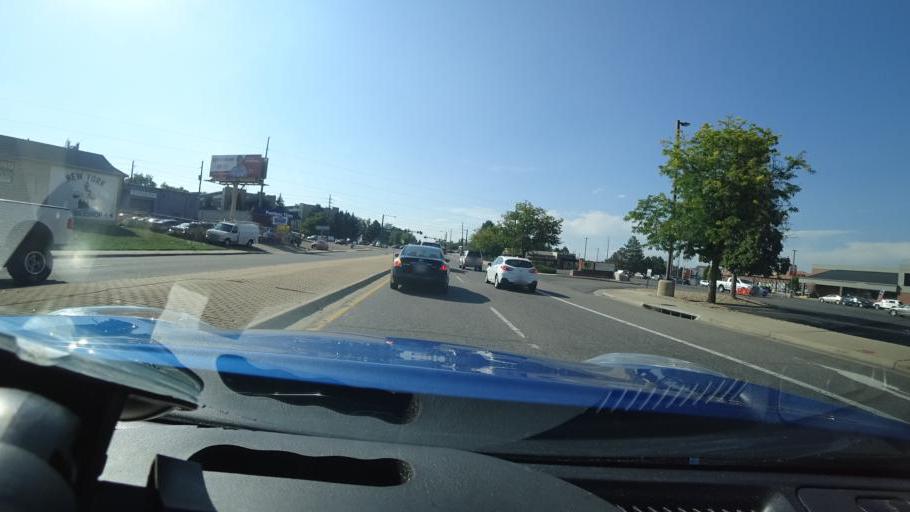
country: US
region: Colorado
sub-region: Arapahoe County
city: Glendale
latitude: 39.6756
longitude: -104.9023
